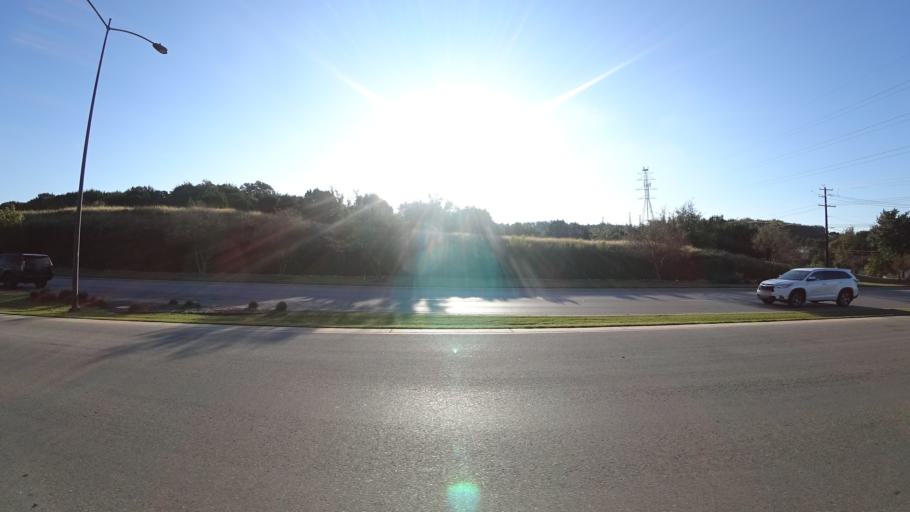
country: US
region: Texas
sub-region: Travis County
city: Hudson Bend
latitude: 30.3715
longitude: -97.8878
